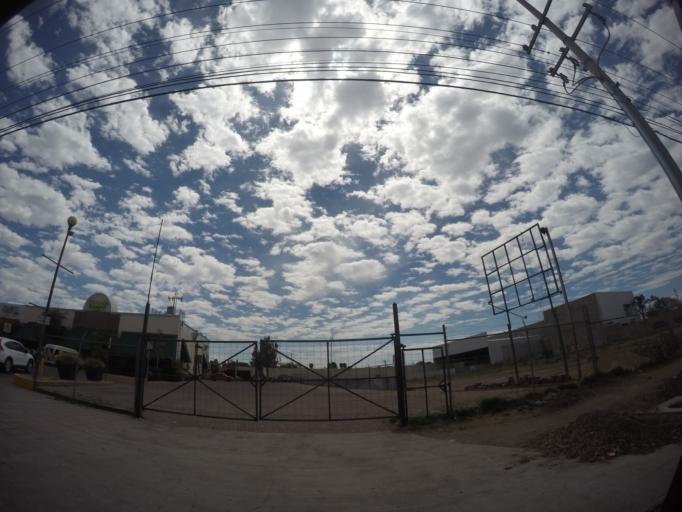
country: MX
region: Guanajuato
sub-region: Leon
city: San Jose de Duran (Los Troncoso)
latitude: 21.0947
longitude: -101.6639
